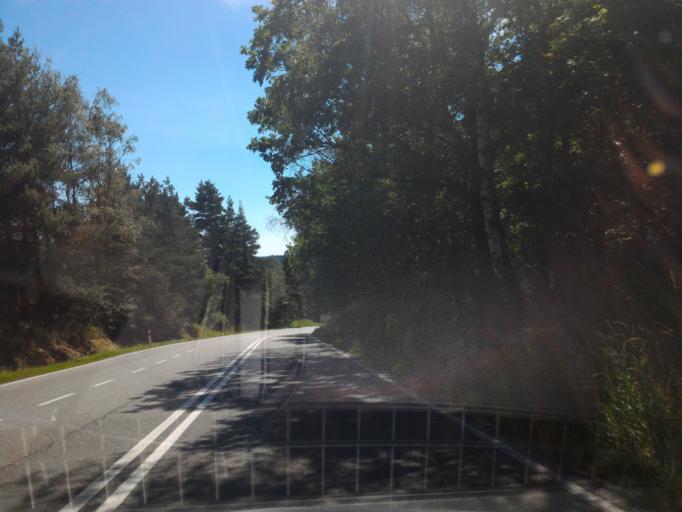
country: CZ
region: Vysocina
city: Dolni Cerekev
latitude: 49.3672
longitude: 15.4973
